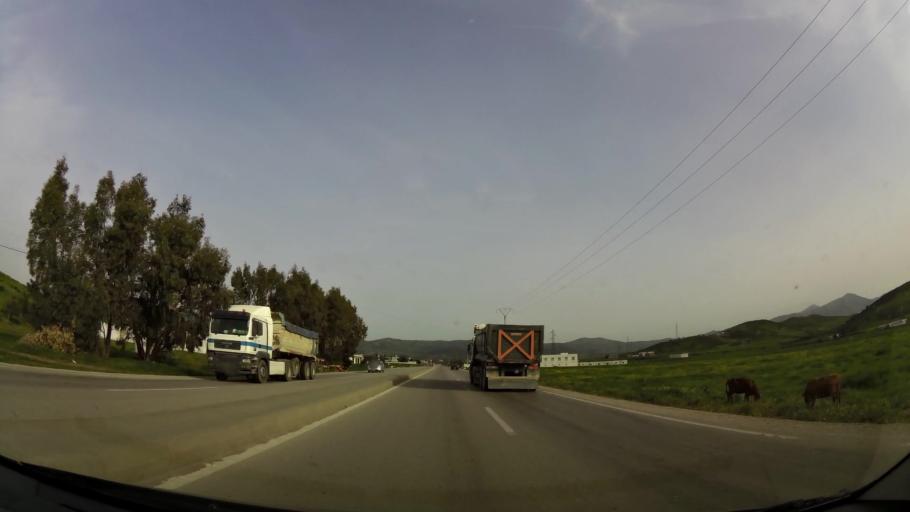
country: MA
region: Tanger-Tetouan
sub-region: Tanger-Assilah
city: Dar Chaoui
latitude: 35.5820
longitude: -5.6375
